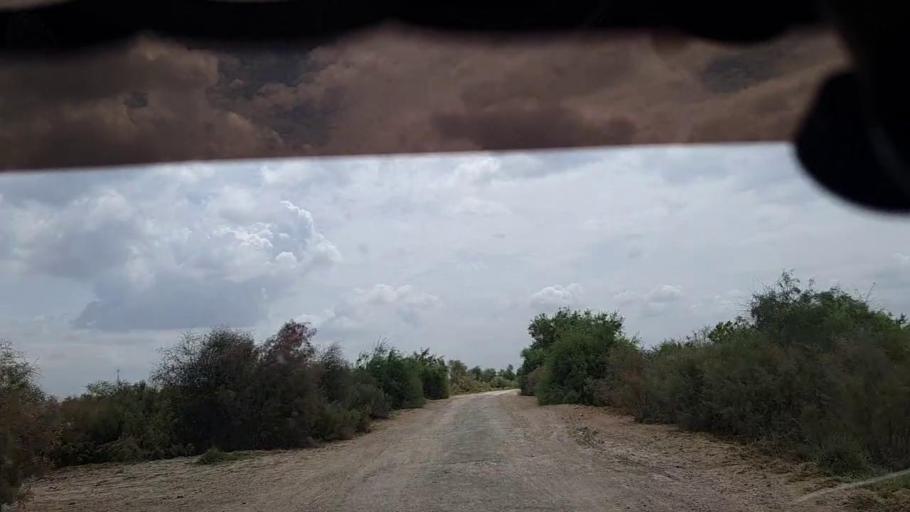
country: PK
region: Sindh
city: Ghauspur
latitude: 28.0623
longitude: 68.9404
